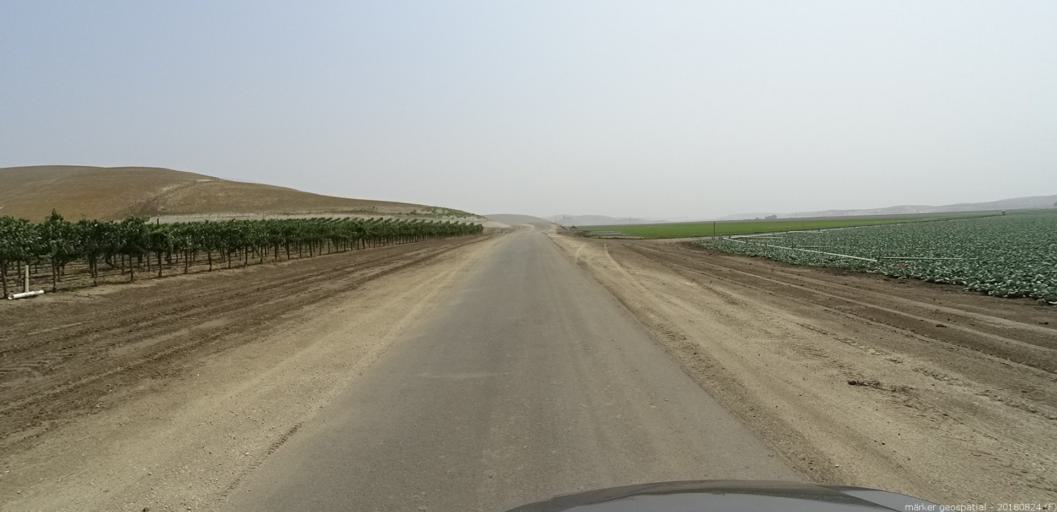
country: US
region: California
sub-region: Monterey County
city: King City
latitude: 36.1910
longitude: -121.0522
